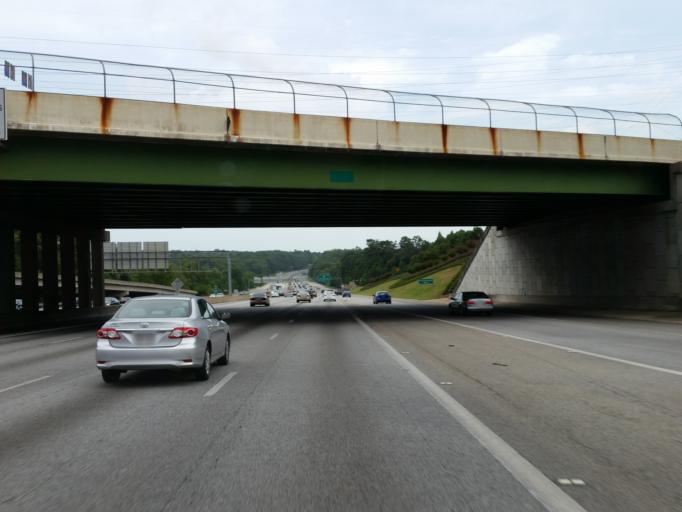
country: US
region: Georgia
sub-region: Cobb County
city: Vinings
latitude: 33.8812
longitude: -84.4536
